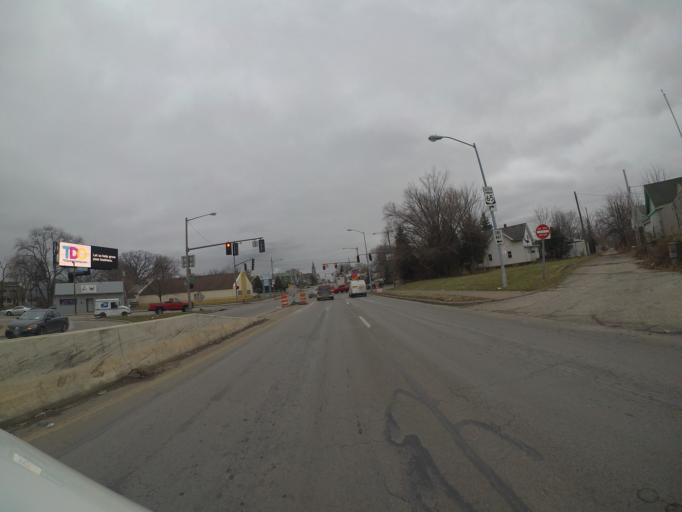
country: US
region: Ohio
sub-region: Lucas County
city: Toledo
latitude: 41.6405
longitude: -83.5260
